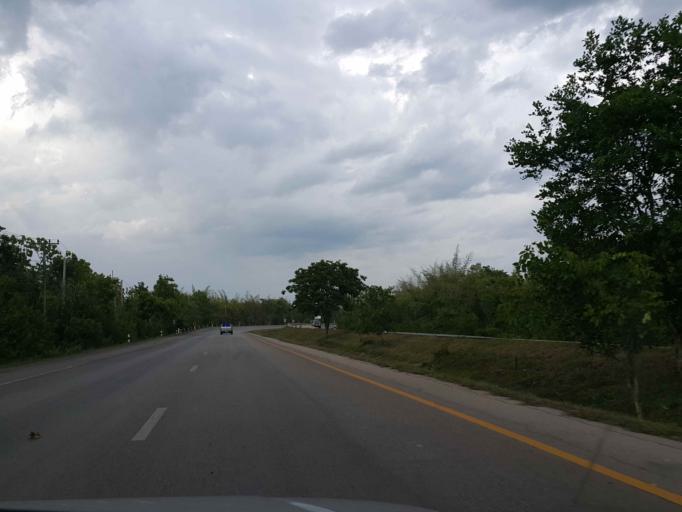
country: TH
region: Lampang
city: Sop Prap
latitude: 17.9656
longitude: 99.3531
